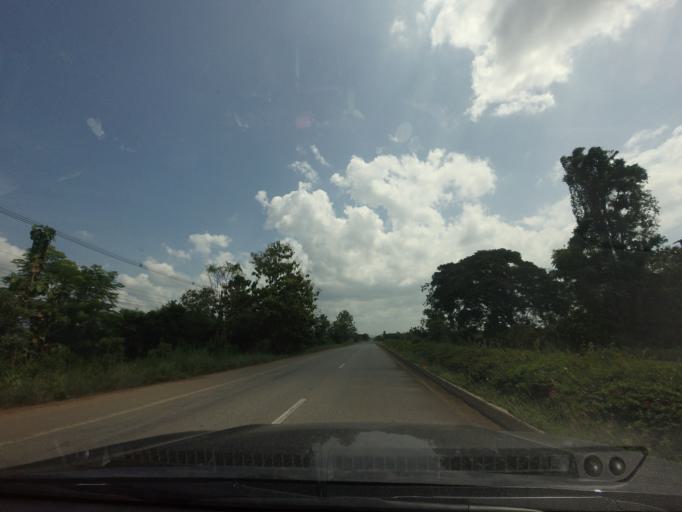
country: TH
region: Phetchabun
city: Phetchabun
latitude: 16.2427
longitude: 101.0752
